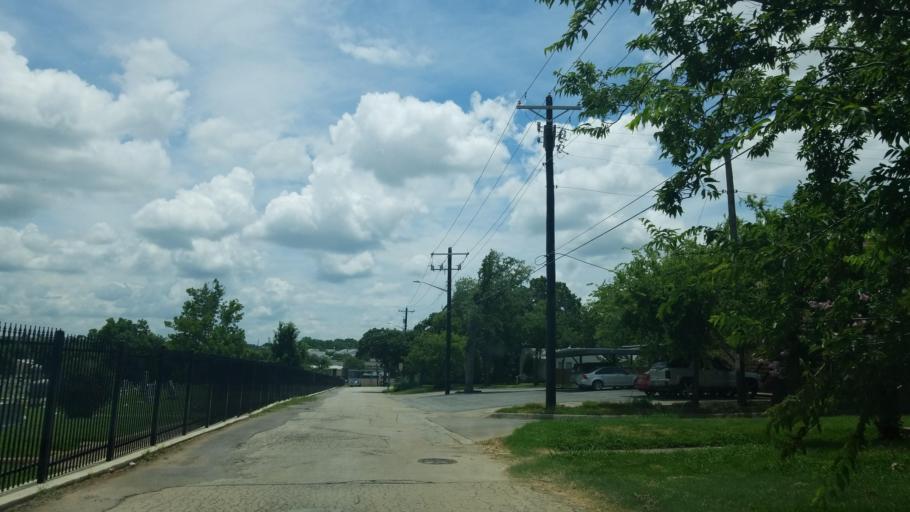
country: US
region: Texas
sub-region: Denton County
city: Denton
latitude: 33.2087
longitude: -97.1403
